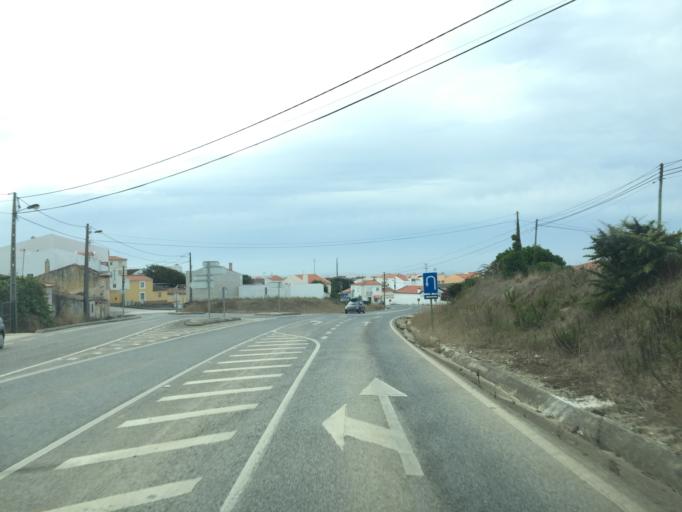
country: PT
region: Leiria
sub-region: Peniche
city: Atouguia da Baleia
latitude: 39.3371
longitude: -9.3136
